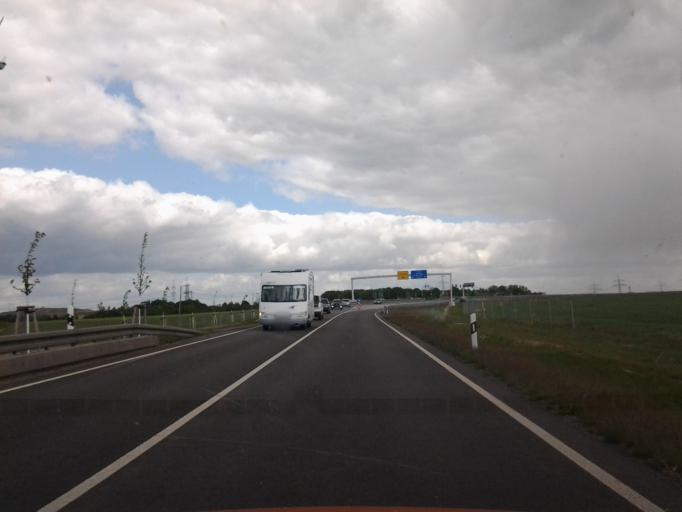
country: DE
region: Berlin
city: Wartenberg
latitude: 52.6109
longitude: 13.5330
